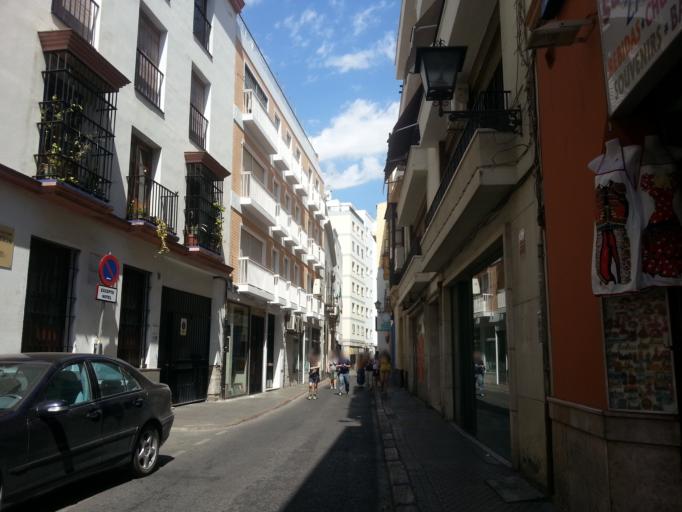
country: ES
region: Andalusia
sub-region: Provincia de Sevilla
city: Sevilla
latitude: 37.3888
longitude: -5.9984
